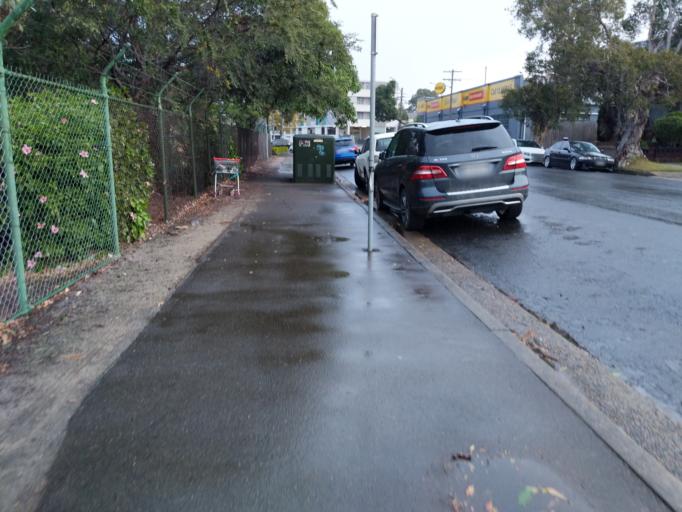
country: AU
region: New South Wales
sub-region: Ashfield
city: Croydon
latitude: -33.8685
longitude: 151.1082
